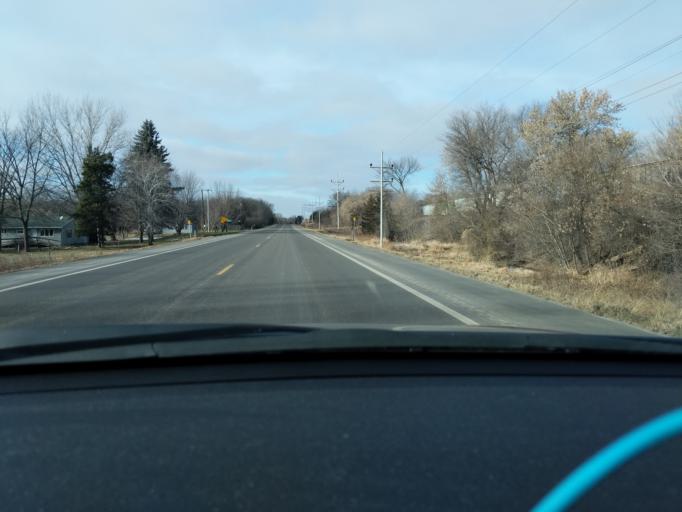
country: US
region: Minnesota
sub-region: Chippewa County
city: Montevideo
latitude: 44.9201
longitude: -95.6991
